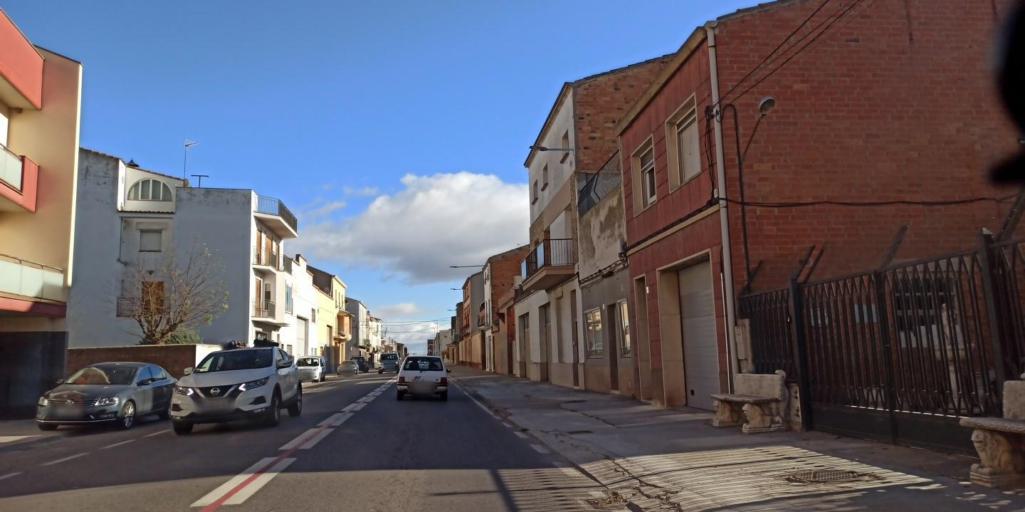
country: ES
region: Catalonia
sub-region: Provincia de Lleida
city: Bellcaire d'Urgell
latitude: 41.7601
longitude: 0.8996
